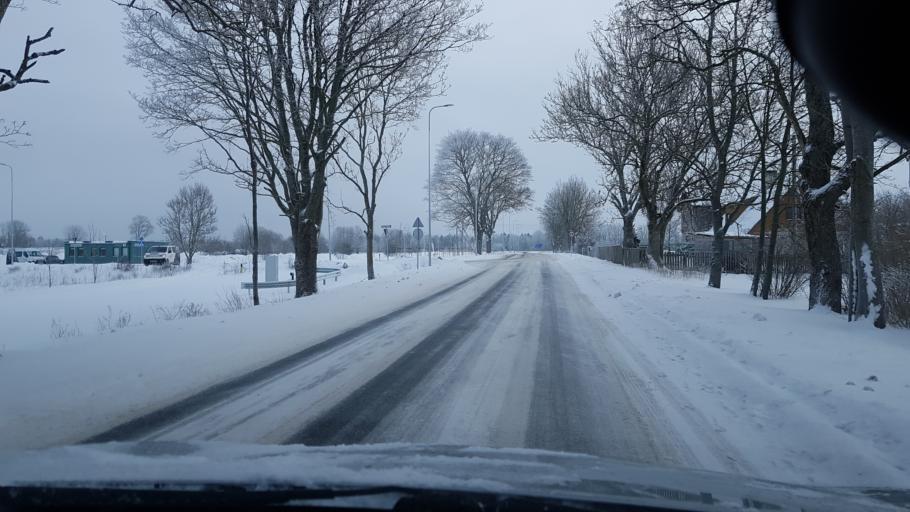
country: EE
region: Harju
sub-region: Keila linn
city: Keila
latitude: 59.3228
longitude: 24.4532
